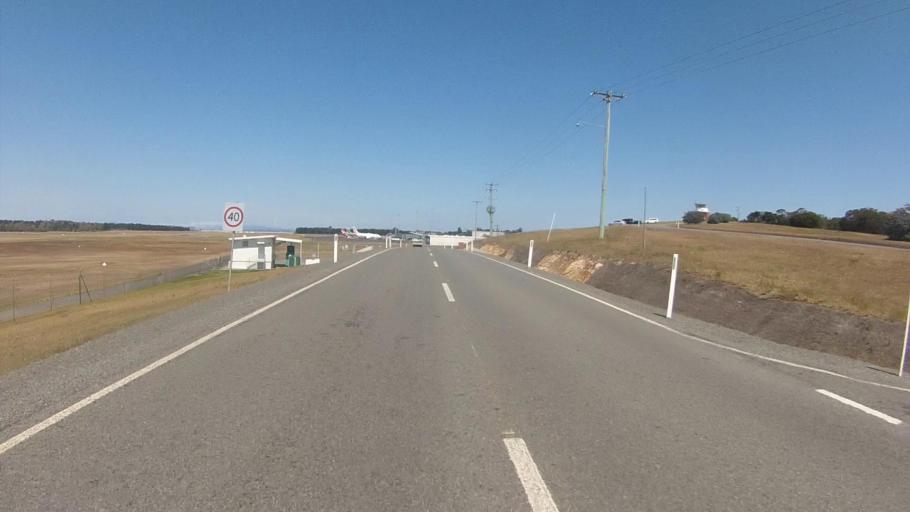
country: AU
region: Tasmania
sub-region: Clarence
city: Seven Mile Beach
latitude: -42.8323
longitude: 147.5012
